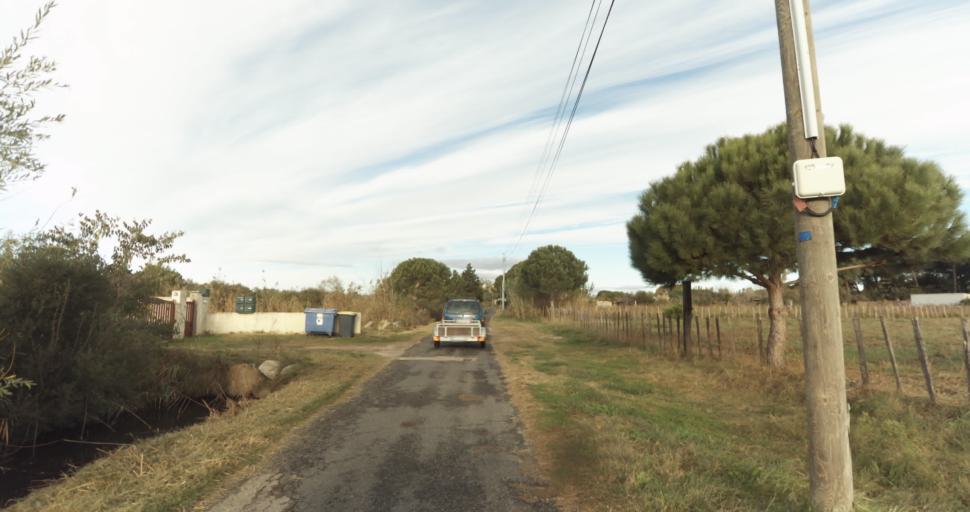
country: FR
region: Languedoc-Roussillon
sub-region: Departement du Gard
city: Aigues-Mortes
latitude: 43.5609
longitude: 4.1997
